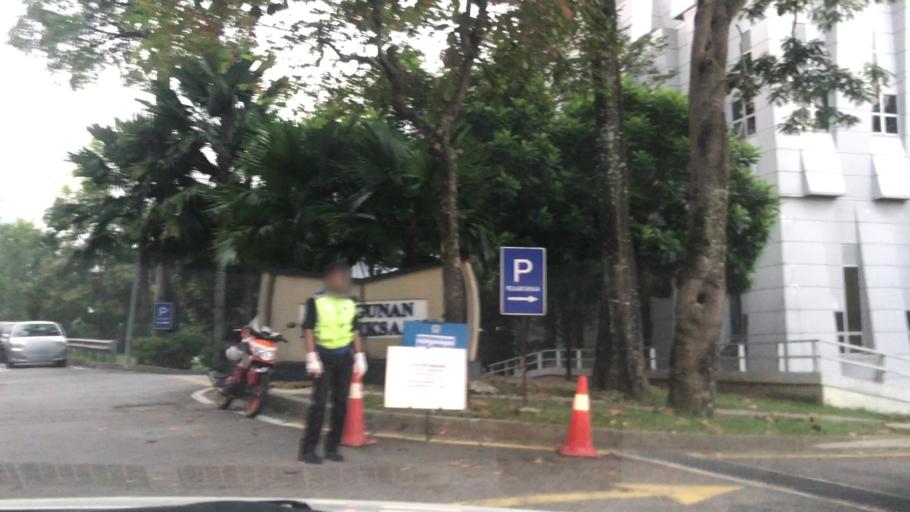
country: MY
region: Kuala Lumpur
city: Kuala Lumpur
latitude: 3.1161
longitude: 101.6589
